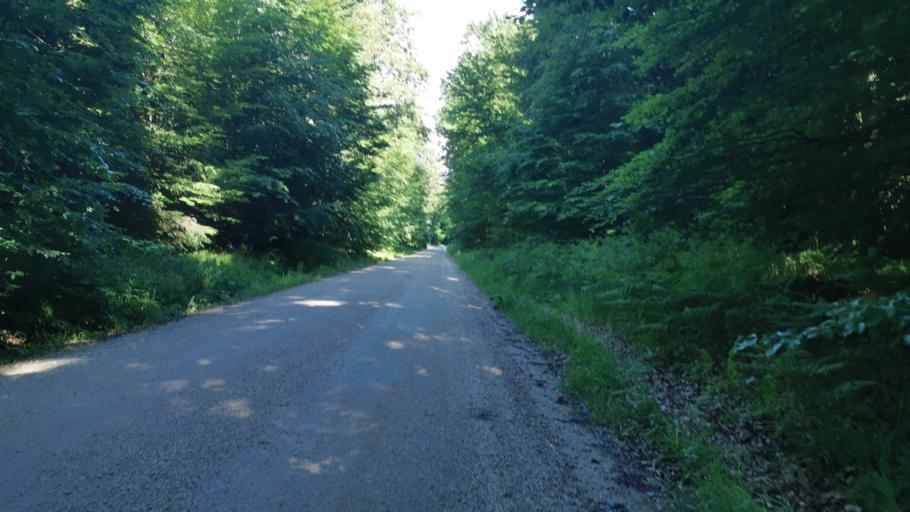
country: DE
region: Bavaria
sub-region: Lower Bavaria
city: Aiglsbach
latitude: 48.7291
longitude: 11.7642
